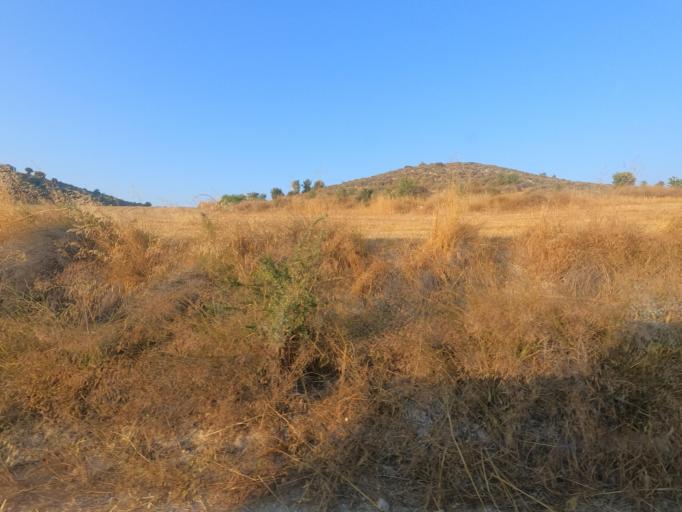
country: CY
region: Larnaka
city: Tersefanou
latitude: 34.9036
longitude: 33.5104
